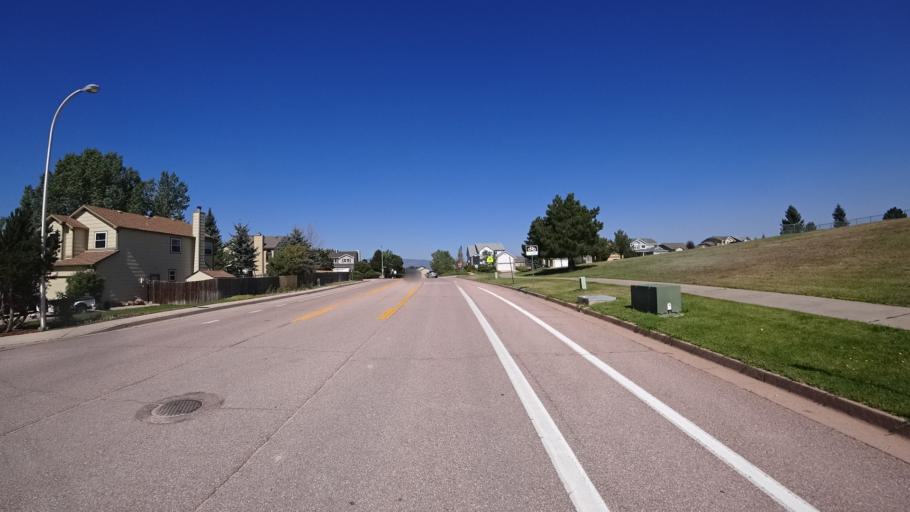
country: US
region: Colorado
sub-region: El Paso County
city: Black Forest
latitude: 38.9601
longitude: -104.7401
